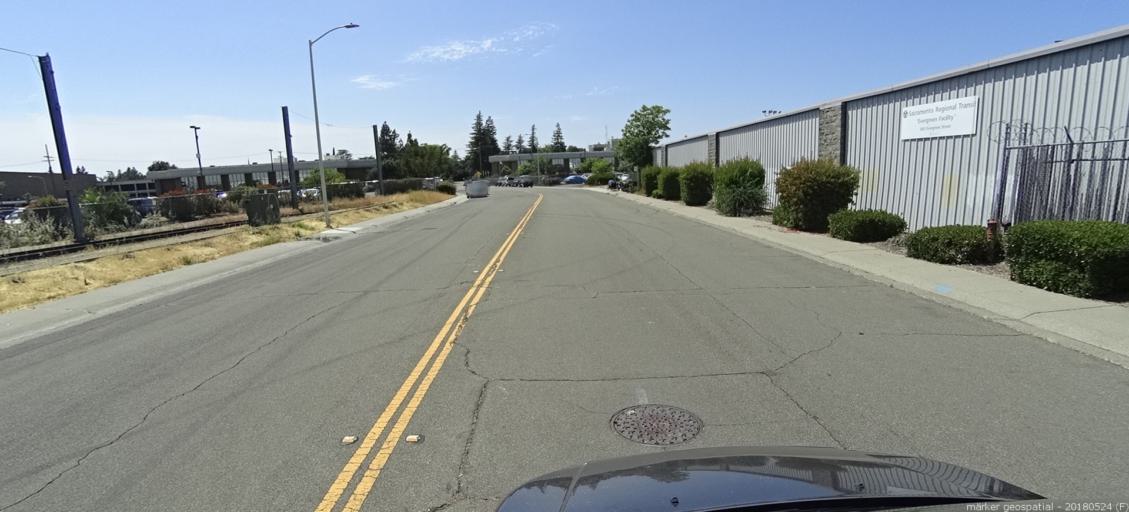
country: US
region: California
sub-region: Sacramento County
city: Sacramento
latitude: 38.6046
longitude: -121.4455
